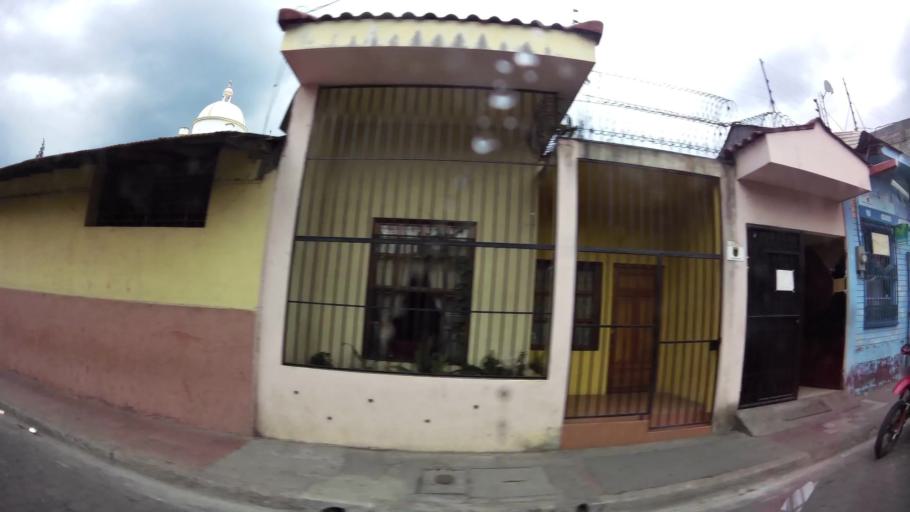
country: NI
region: Jinotega
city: Jinotega
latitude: 13.0915
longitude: -86.0023
